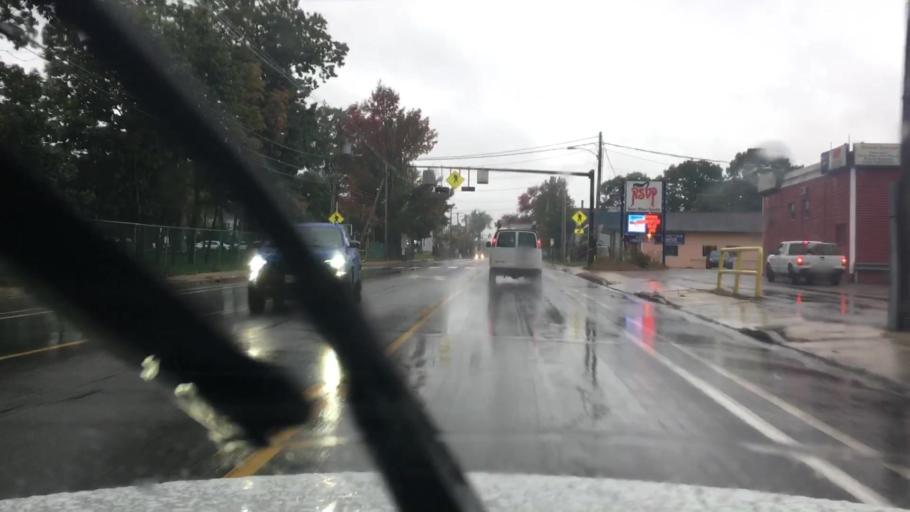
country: US
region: Maine
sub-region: Cumberland County
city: Portland
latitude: 43.6779
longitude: -70.2879
